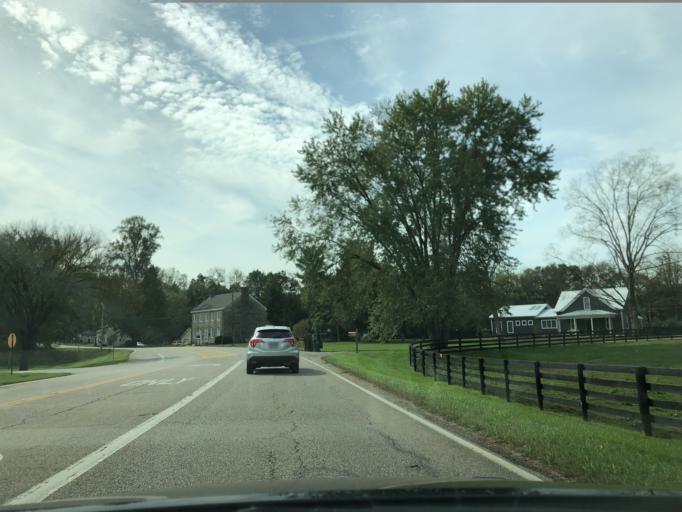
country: US
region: Ohio
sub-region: Clermont County
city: Milford
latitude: 39.1928
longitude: -84.2892
